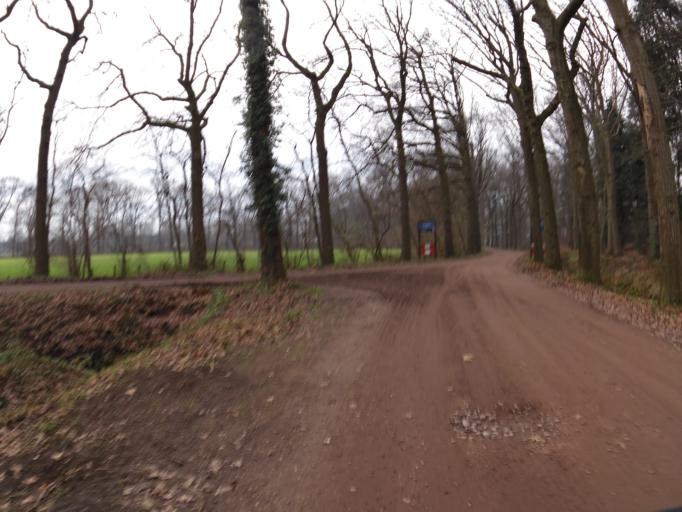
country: NL
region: North Brabant
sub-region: Gemeente Vught
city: Vught
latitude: 51.6390
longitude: 5.2986
